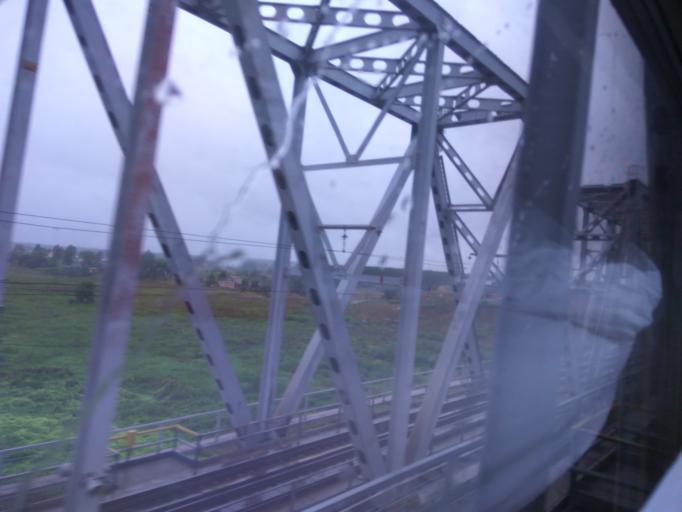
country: RU
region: Moskovskaya
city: Kashira
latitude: 54.8621
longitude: 38.1642
